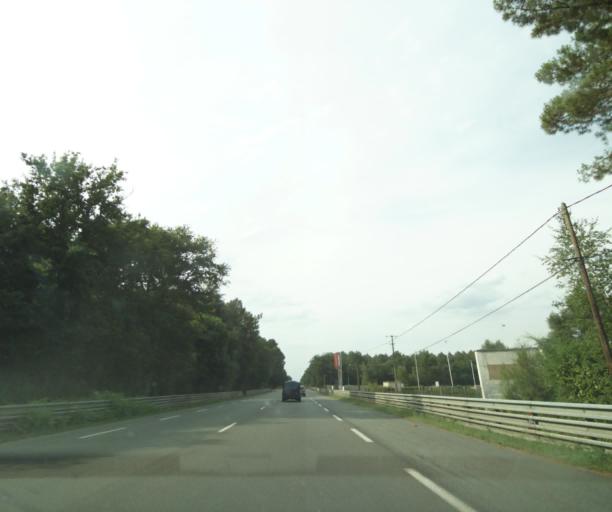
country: FR
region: Pays de la Loire
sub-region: Departement de la Sarthe
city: Mulsanne
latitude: 47.9325
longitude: 0.2393
